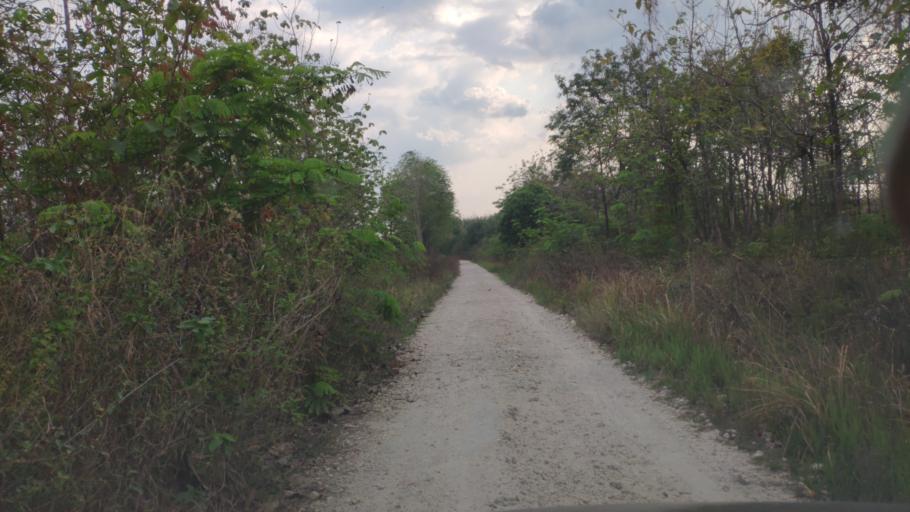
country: ID
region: Central Java
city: Randublatung
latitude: -7.2803
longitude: 111.2829
